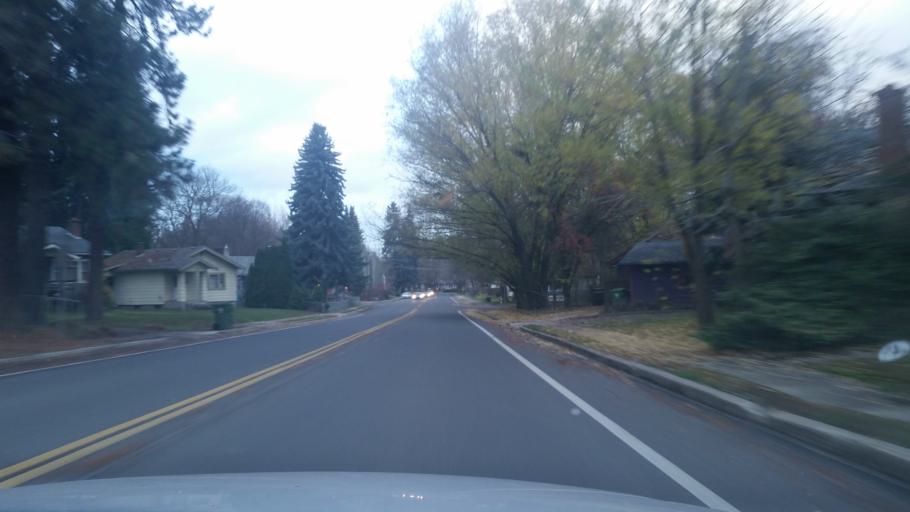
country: US
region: Washington
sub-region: Spokane County
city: Spokane
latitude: 47.6420
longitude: -117.3952
